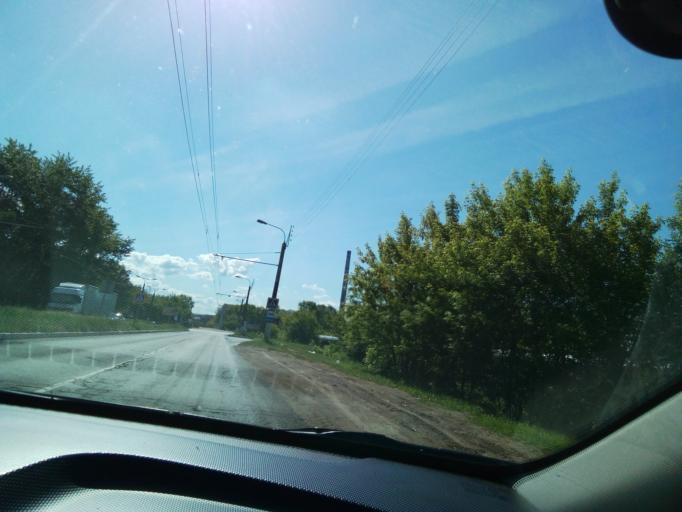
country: RU
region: Chuvashia
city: Novocheboksarsk
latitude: 56.0920
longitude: 47.4994
